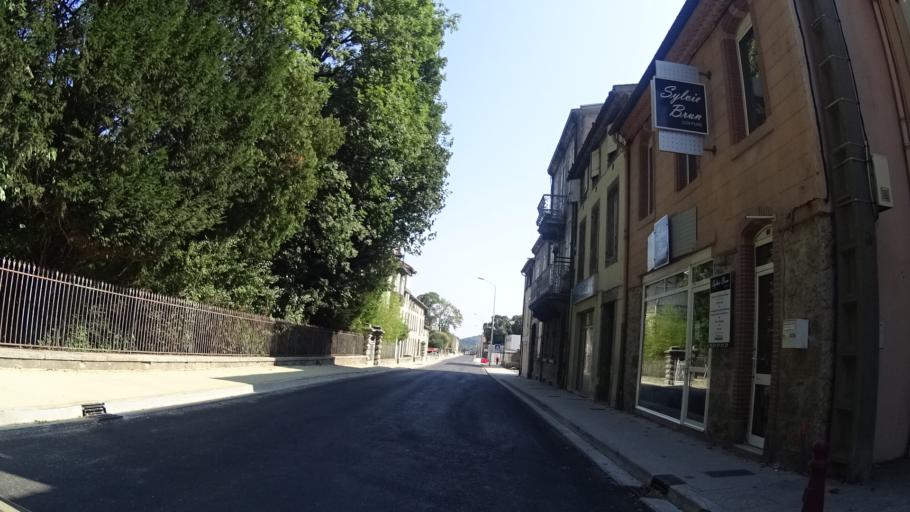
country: FR
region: Midi-Pyrenees
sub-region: Departement de l'Ariege
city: Lavelanet
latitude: 42.9358
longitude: 1.8508
